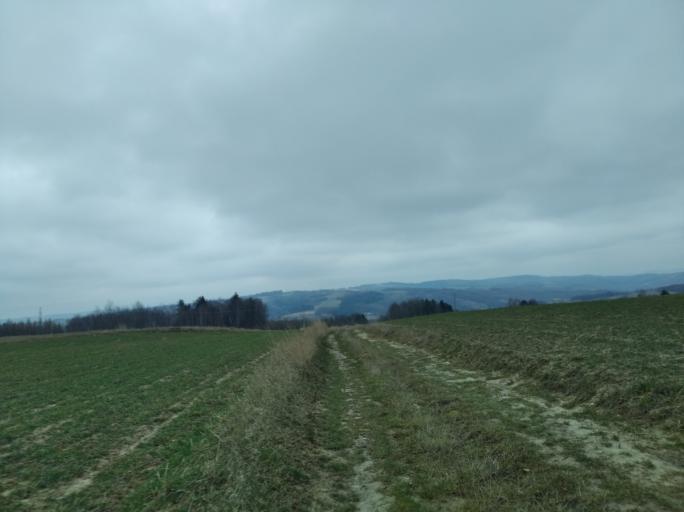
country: PL
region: Subcarpathian Voivodeship
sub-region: Powiat strzyzowski
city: Strzyzow
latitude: 49.9051
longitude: 21.8069
